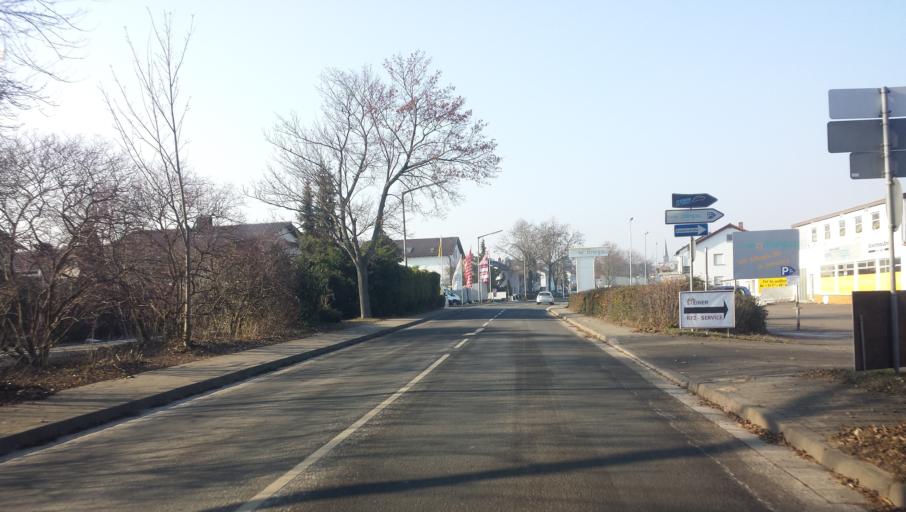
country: DE
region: Rheinland-Pfalz
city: Monsheim
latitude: 49.6345
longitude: 8.2184
